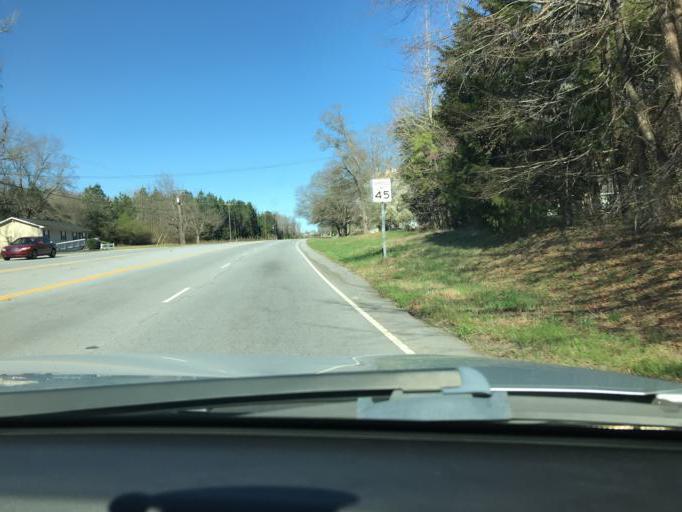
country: US
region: South Carolina
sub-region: Laurens County
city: Clinton
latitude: 34.4732
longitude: -81.9297
